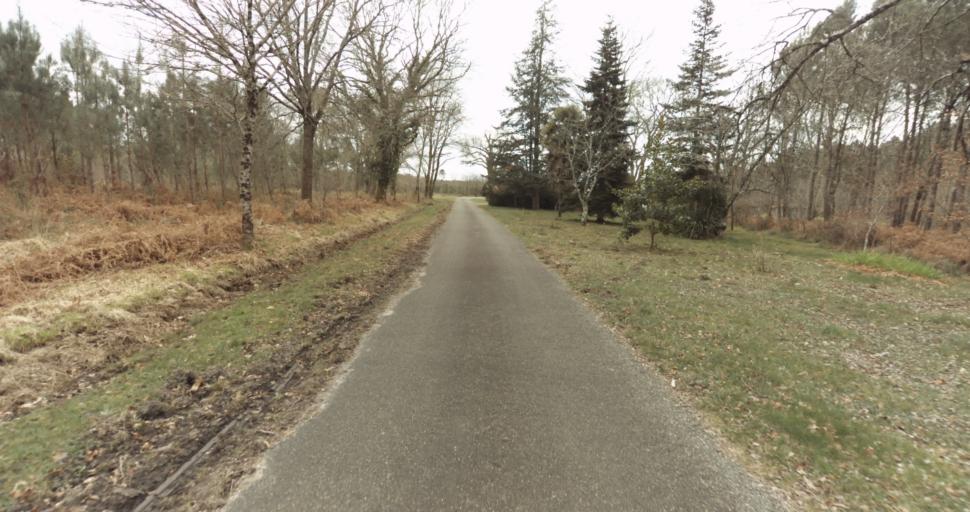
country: FR
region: Aquitaine
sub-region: Departement des Landes
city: Roquefort
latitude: 44.0810
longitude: -0.3888
